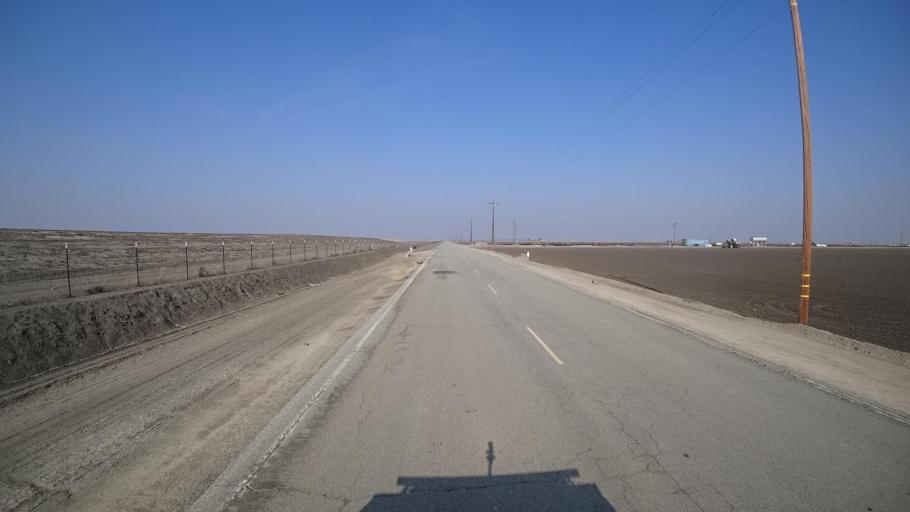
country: US
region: California
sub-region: Kern County
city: Buttonwillow
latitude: 35.3173
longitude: -119.3768
